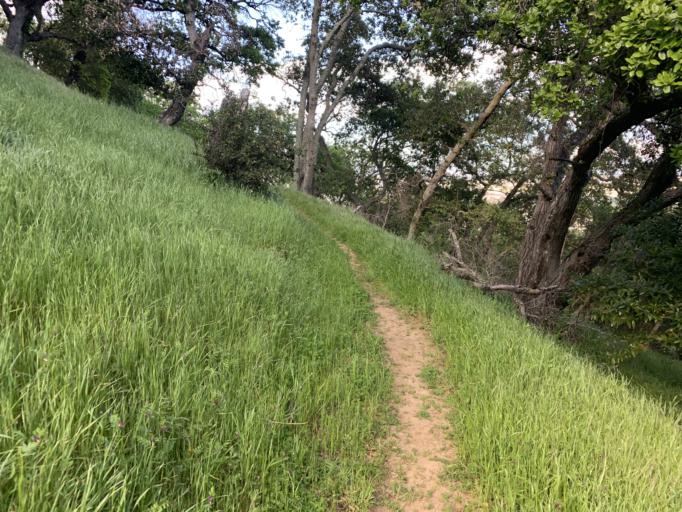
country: US
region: California
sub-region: Contra Costa County
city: Martinez
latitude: 38.0114
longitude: -122.1474
